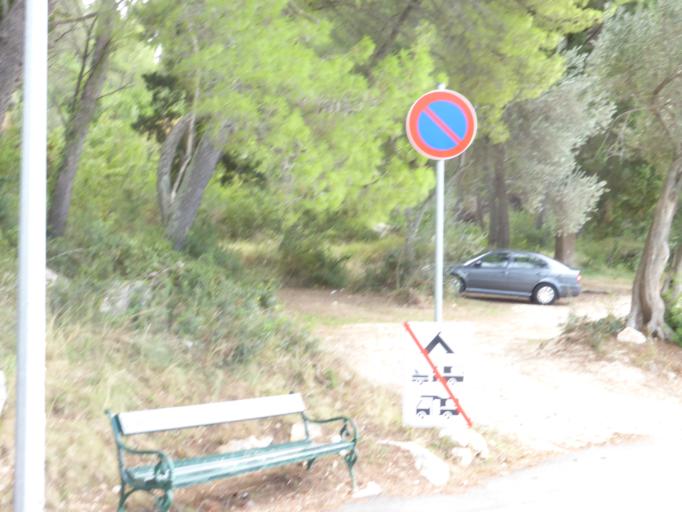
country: HR
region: Dubrovacko-Neretvanska
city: Podgora
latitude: 42.7796
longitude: 17.8850
